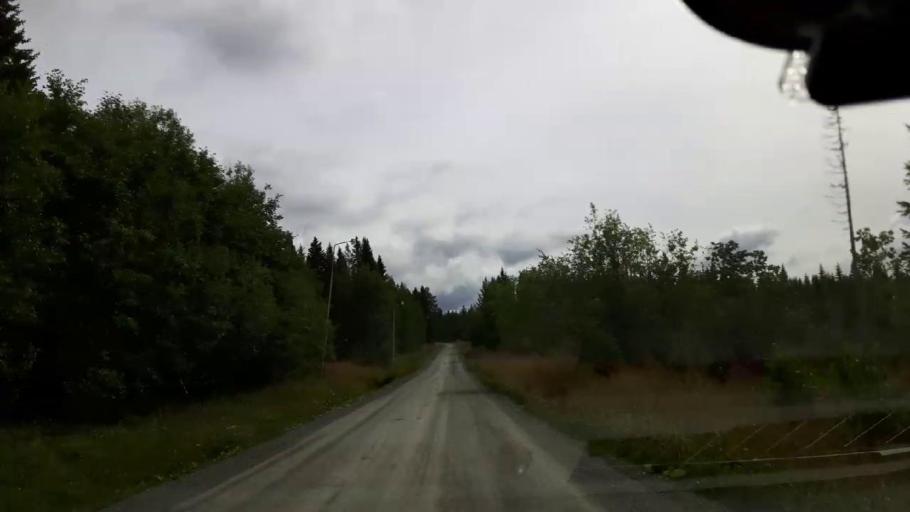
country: SE
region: Jaemtland
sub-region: Krokoms Kommun
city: Valla
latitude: 63.6429
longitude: 13.9943
